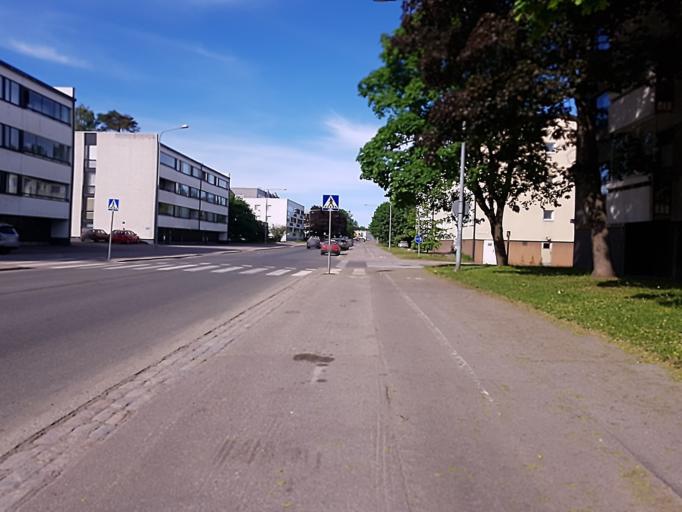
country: FI
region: Uusimaa
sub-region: Helsinki
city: Helsinki
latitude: 60.2254
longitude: 24.9534
